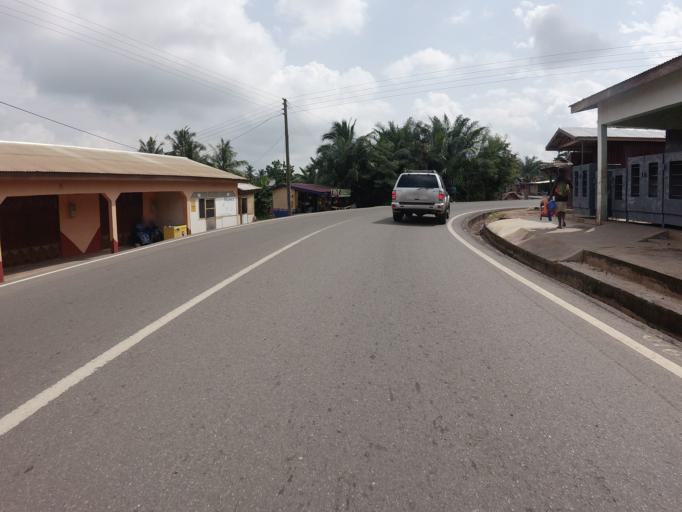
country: GH
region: Volta
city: Ho
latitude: 6.6202
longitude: 0.4772
